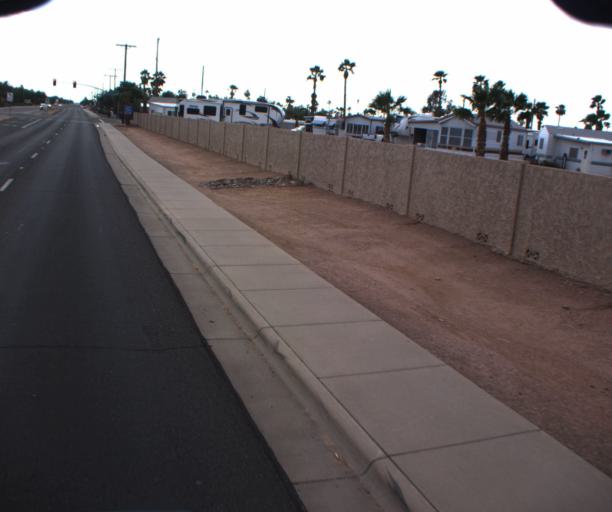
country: US
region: Arizona
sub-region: Pinal County
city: Apache Junction
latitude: 33.4089
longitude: -111.5462
